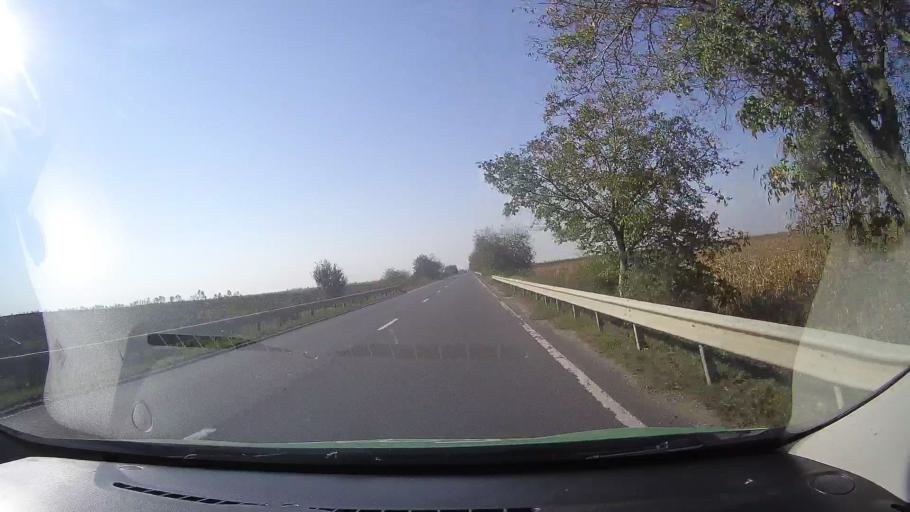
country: RO
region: Satu Mare
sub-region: Comuna Petresti
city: Petresti
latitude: 47.6281
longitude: 22.3902
